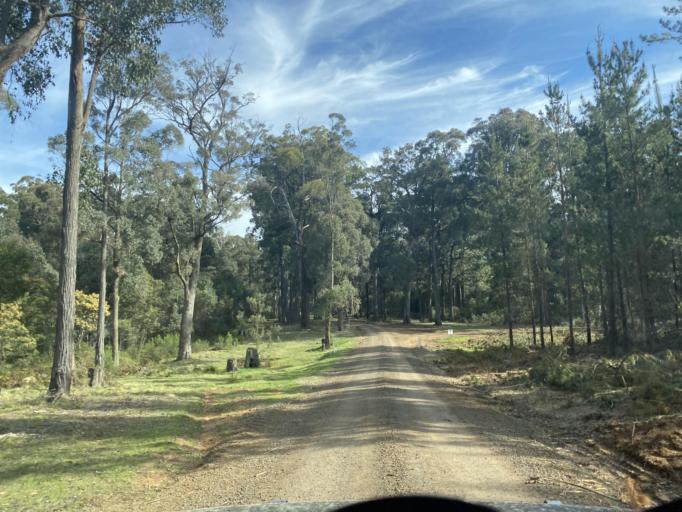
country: AU
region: Victoria
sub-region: Mansfield
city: Mansfield
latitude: -36.8428
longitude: 146.1824
